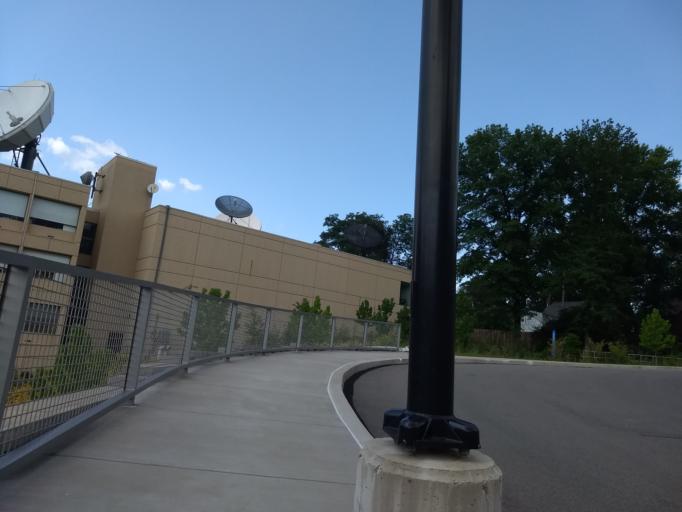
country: US
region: Pennsylvania
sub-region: Allegheny County
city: Bloomfield
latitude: 40.4460
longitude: -79.9449
